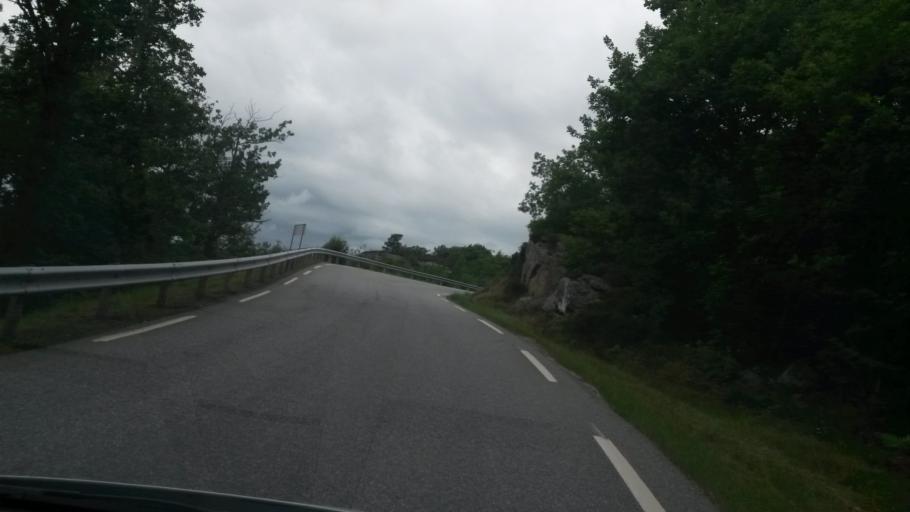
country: NO
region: Rogaland
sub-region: Sandnes
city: Sandnes
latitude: 58.8940
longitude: 5.7756
